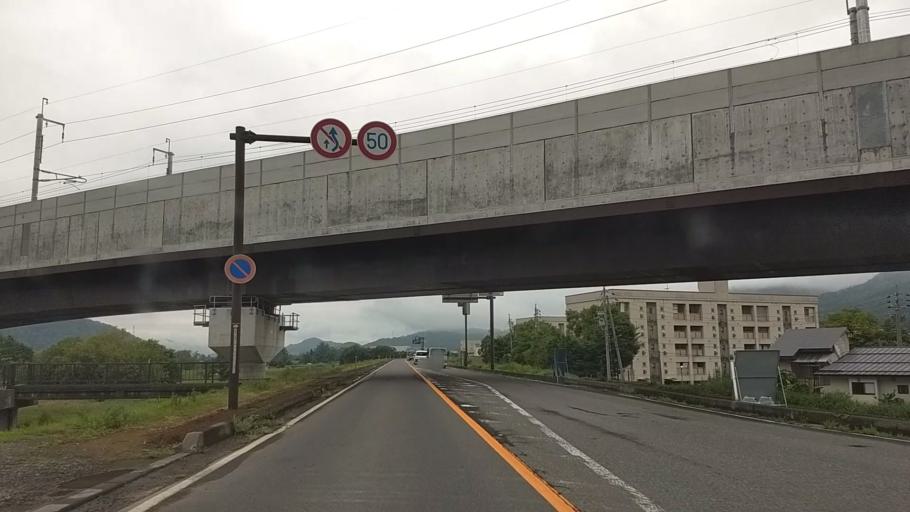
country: JP
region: Nagano
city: Iiyama
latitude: 36.8417
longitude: 138.3627
